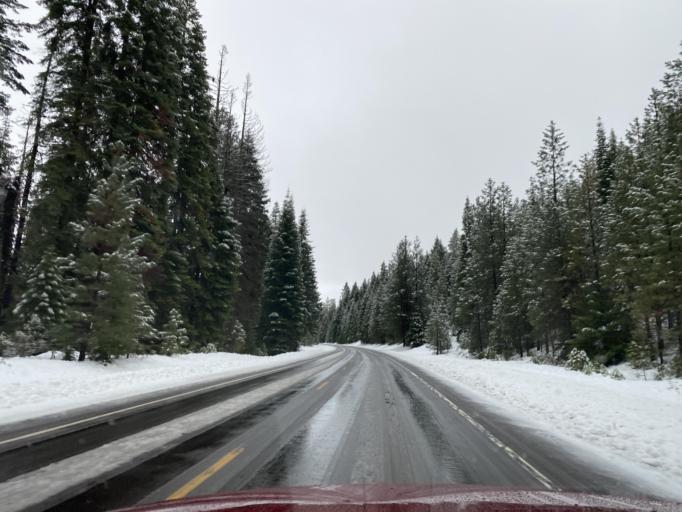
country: US
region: Oregon
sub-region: Klamath County
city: Klamath Falls
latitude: 42.5374
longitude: -122.0903
